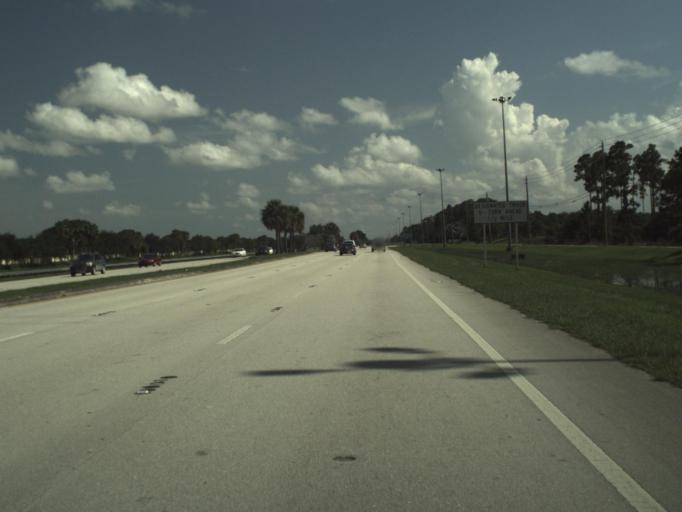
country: US
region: Florida
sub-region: Palm Beach County
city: Wellington
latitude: 26.5825
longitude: -80.2061
